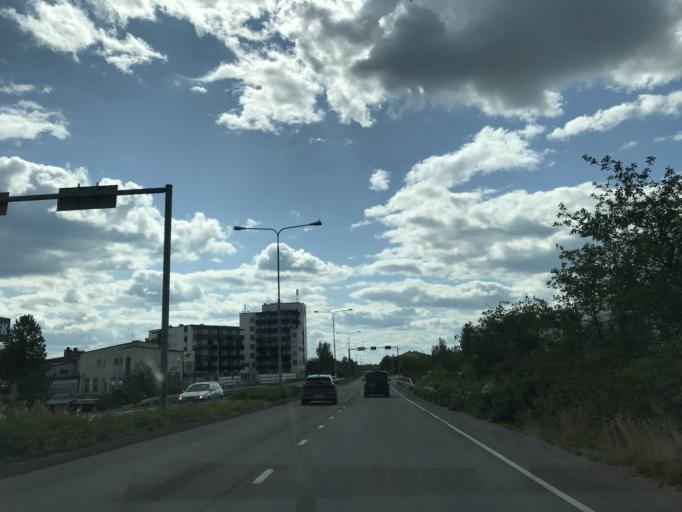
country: FI
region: Uusimaa
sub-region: Helsinki
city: Maentsaelae
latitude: 60.6371
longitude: 25.3183
